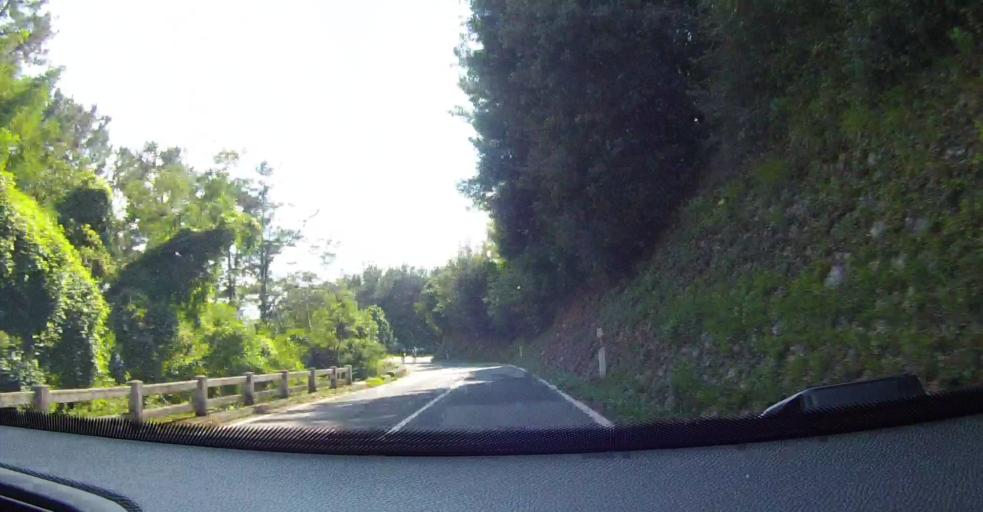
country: ES
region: Basque Country
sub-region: Bizkaia
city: Kortezubi
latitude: 43.3601
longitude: -2.6468
